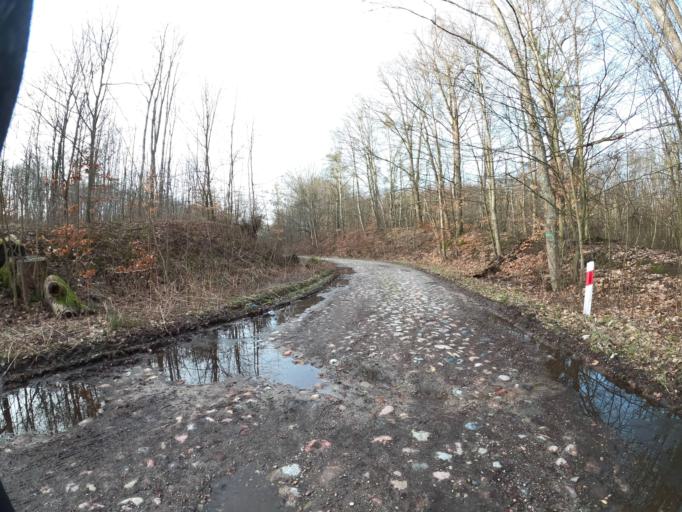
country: PL
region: West Pomeranian Voivodeship
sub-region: Powiat koszalinski
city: Polanow
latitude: 54.1673
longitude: 16.7552
